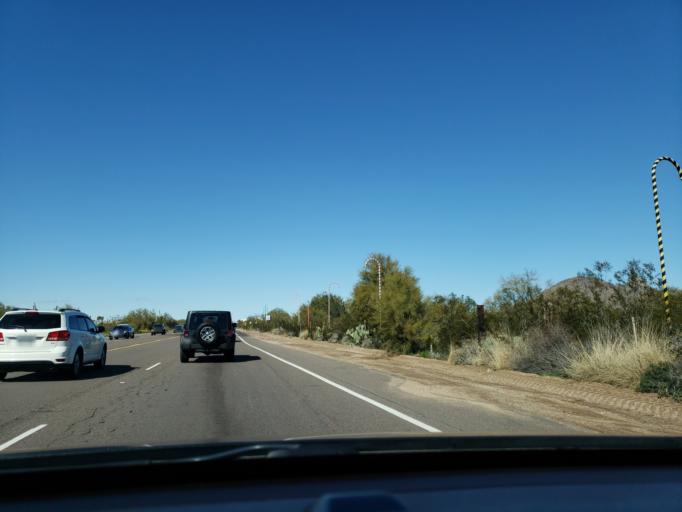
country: US
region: Arizona
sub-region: Maricopa County
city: Carefree
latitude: 33.7026
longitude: -111.8906
